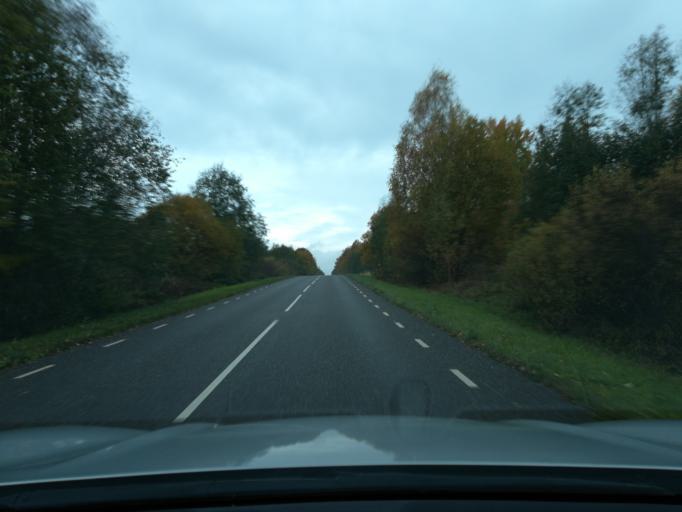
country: EE
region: Ida-Virumaa
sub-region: Johvi vald
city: Johvi
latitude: 59.0612
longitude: 27.3852
